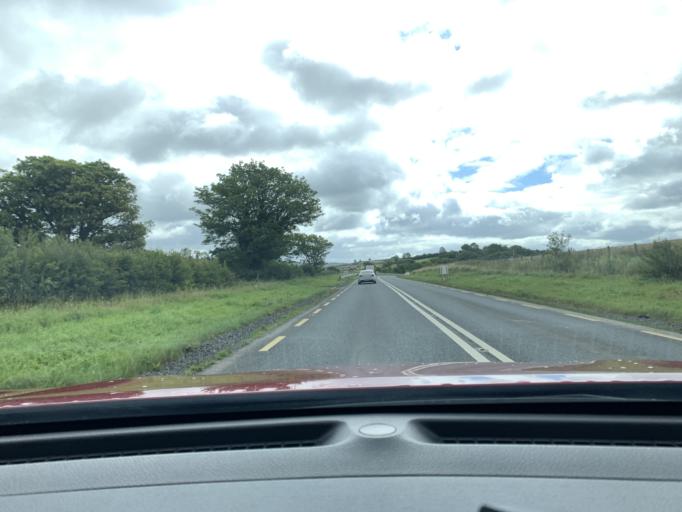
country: IE
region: Connaught
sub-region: Sligo
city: Ballymote
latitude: 54.0990
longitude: -8.4003
